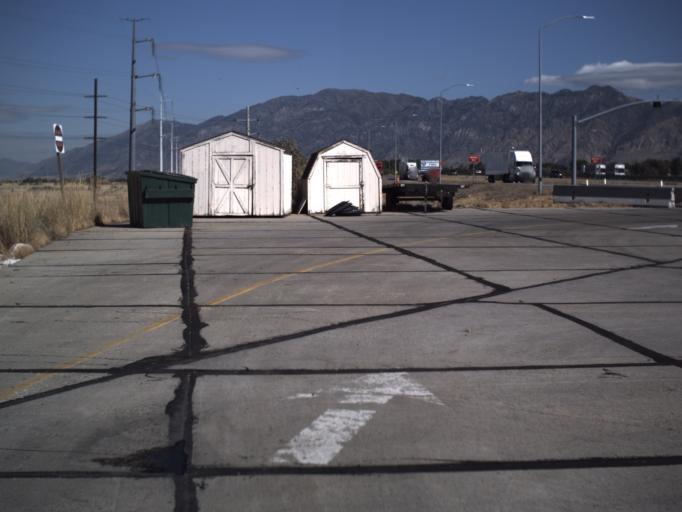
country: US
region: Utah
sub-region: Box Elder County
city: Perry
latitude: 41.4403
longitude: -112.0578
